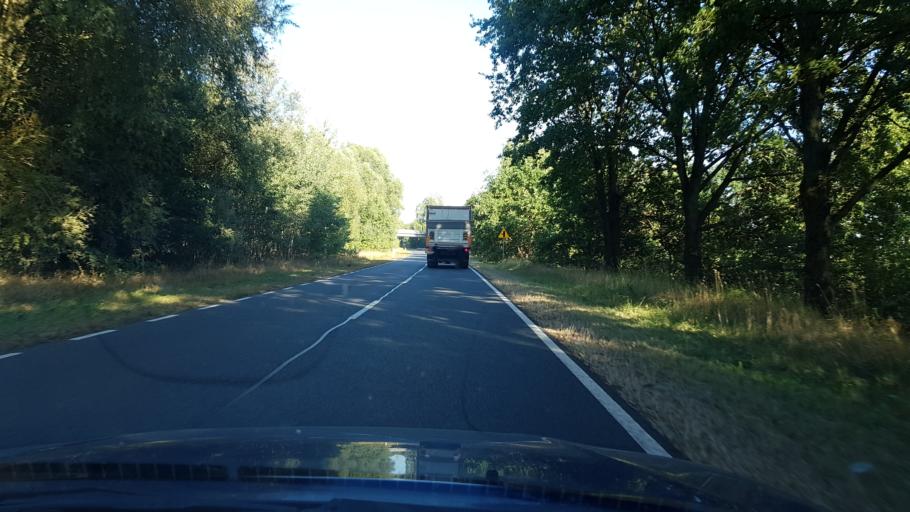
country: PL
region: West Pomeranian Voivodeship
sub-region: Powiat stargardzki
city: Marianowo
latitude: 53.4294
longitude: 15.2215
